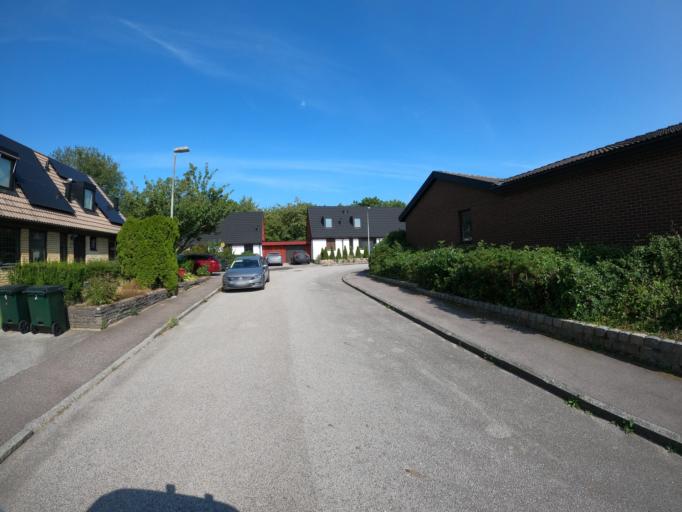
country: SE
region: Skane
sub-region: Lunds Kommun
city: Lund
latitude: 55.7295
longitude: 13.1696
